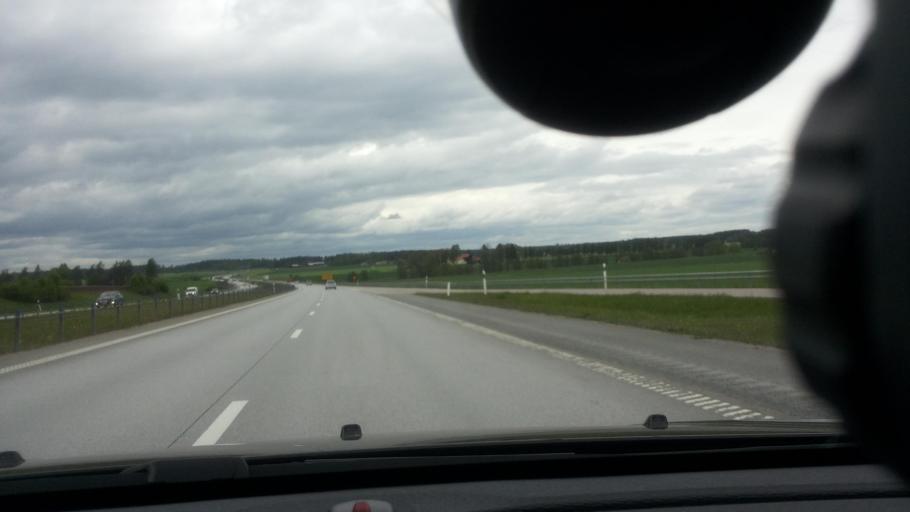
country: SE
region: Uppsala
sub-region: Uppsala Kommun
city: Storvreta
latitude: 59.9428
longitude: 17.6596
